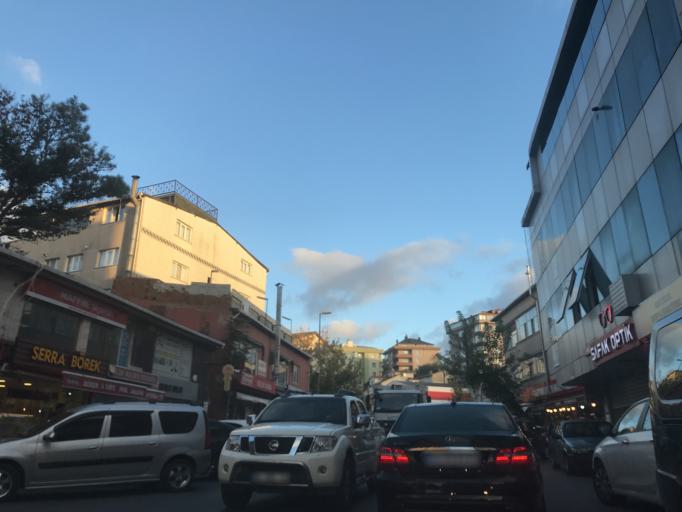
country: TR
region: Istanbul
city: Sisli
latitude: 41.1301
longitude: 29.0420
